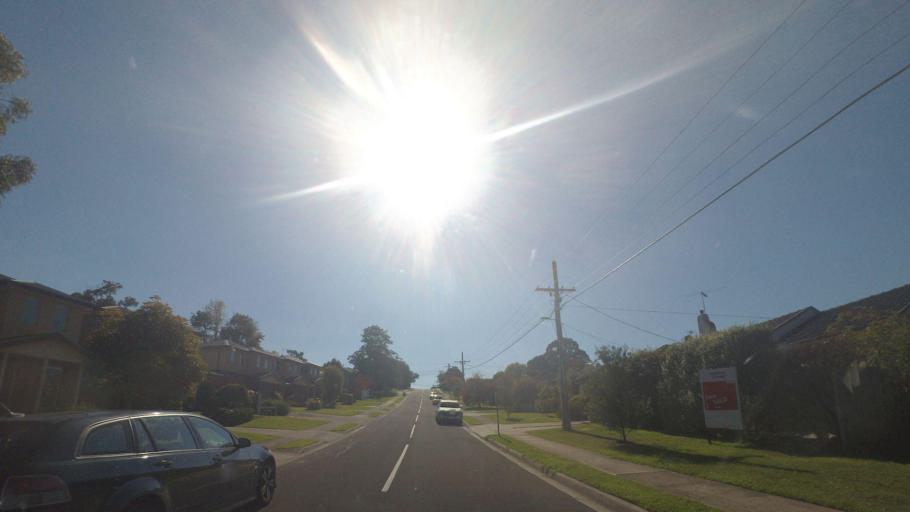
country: AU
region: Victoria
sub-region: Knox
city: Ferntree Gully
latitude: -37.8834
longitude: 145.2817
